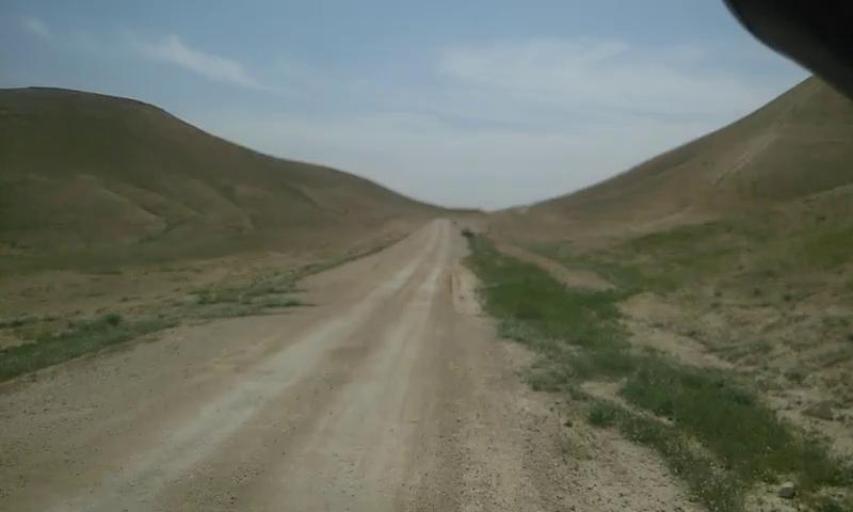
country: PS
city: `Arab ar Rashaydah
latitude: 31.4973
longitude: 35.2940
